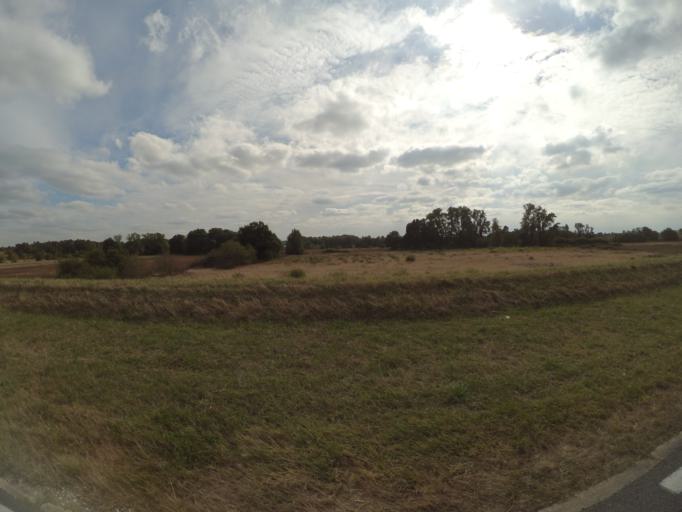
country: FR
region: Centre
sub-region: Departement d'Indre-et-Loire
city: Luynes
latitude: 47.3826
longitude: 0.5792
